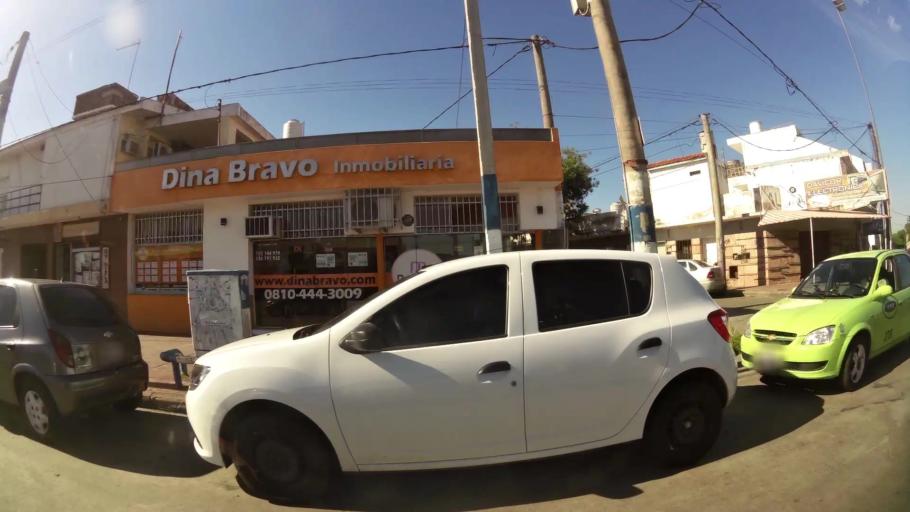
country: AR
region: Cordoba
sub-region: Departamento de Capital
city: Cordoba
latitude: -31.4332
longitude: -64.1577
